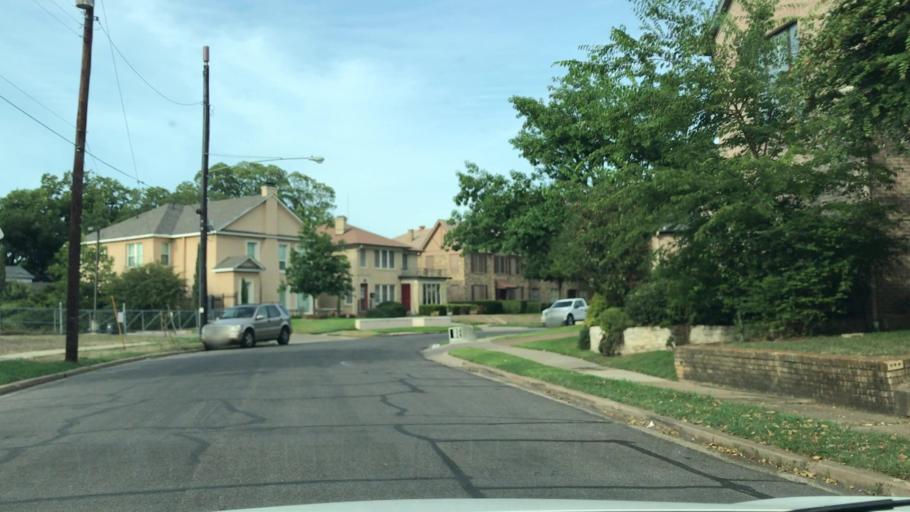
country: US
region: Texas
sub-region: Dallas County
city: Highland Park
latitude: 32.8204
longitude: -96.8095
